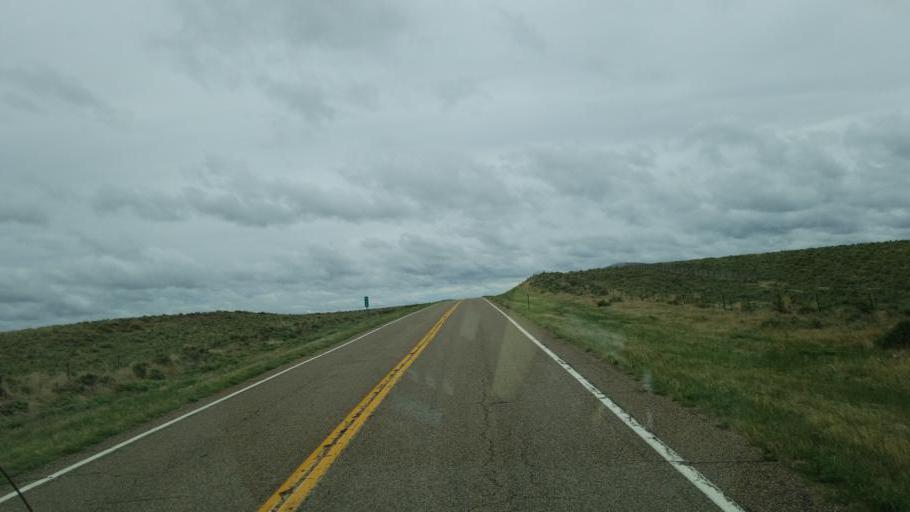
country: US
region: Colorado
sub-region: Lincoln County
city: Hugo
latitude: 38.8501
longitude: -103.5068
